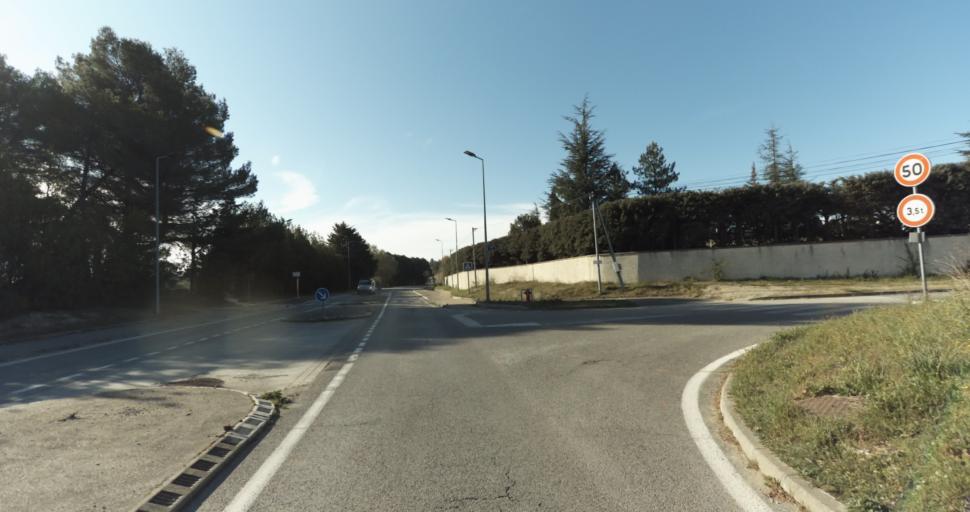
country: FR
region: Provence-Alpes-Cote d'Azur
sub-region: Departement des Bouches-du-Rhone
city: Aix-en-Provence
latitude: 43.5666
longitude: 5.4339
